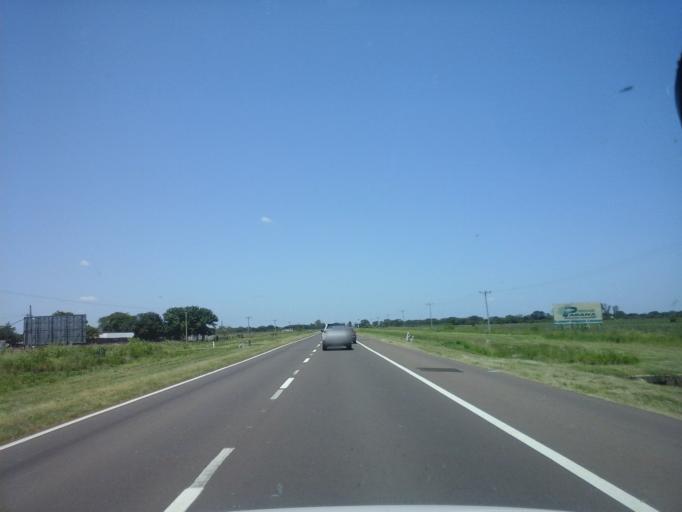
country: AR
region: Corrientes
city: Paso de la Patria
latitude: -27.4154
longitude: -58.6784
